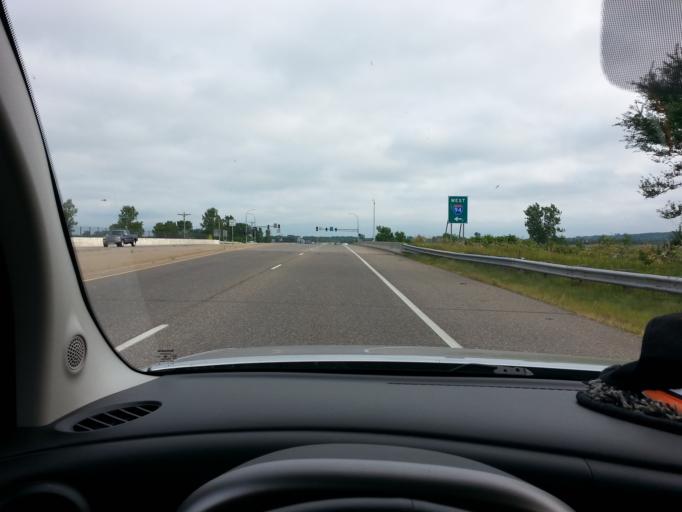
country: US
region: Minnesota
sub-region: Washington County
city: Lake Elmo
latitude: 44.9478
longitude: -92.8624
